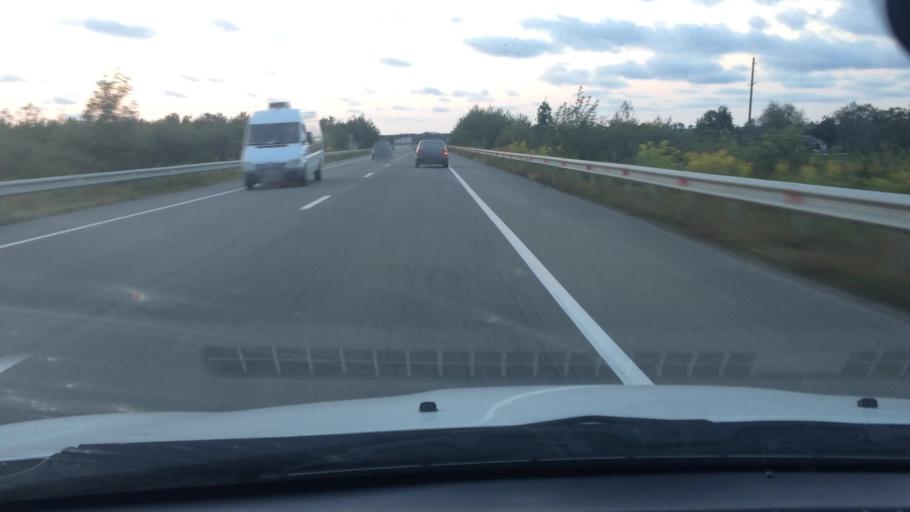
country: GE
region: Ajaria
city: Ochkhamuri
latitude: 41.9074
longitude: 41.7863
